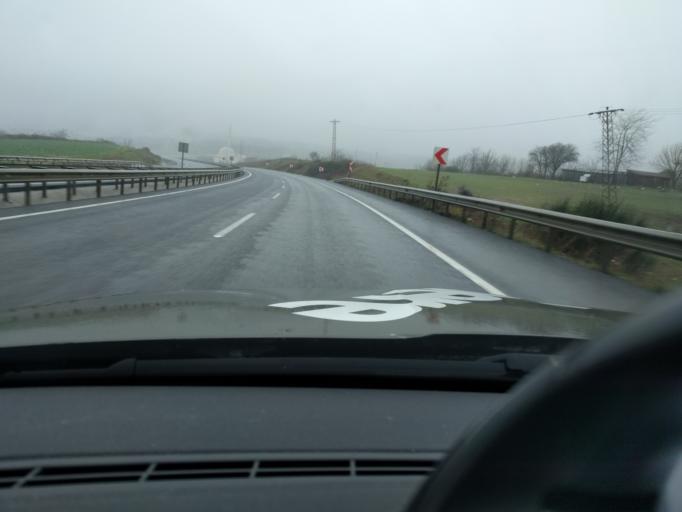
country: TR
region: Istanbul
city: Boyalik
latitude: 41.2747
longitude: 28.6560
